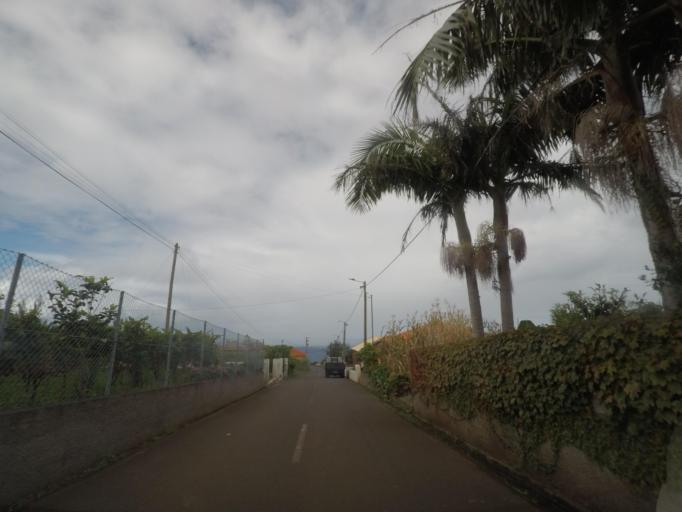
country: PT
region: Madeira
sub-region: Santana
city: Santana
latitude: 32.8332
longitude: -16.9073
